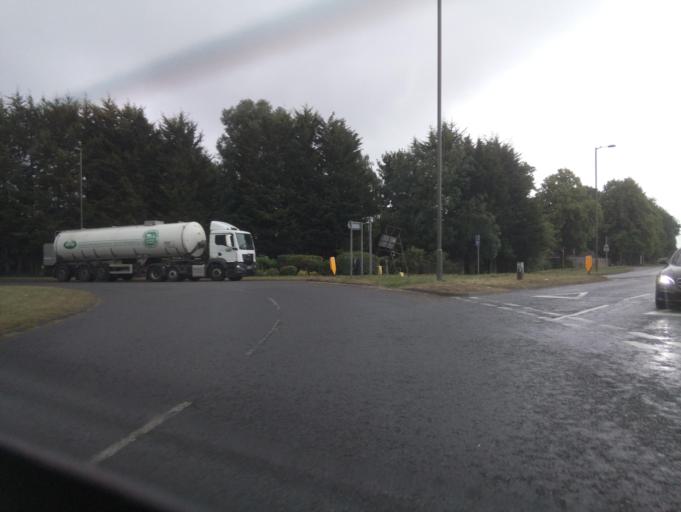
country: GB
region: England
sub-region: Surrey
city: Horley
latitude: 51.1807
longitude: -0.1642
